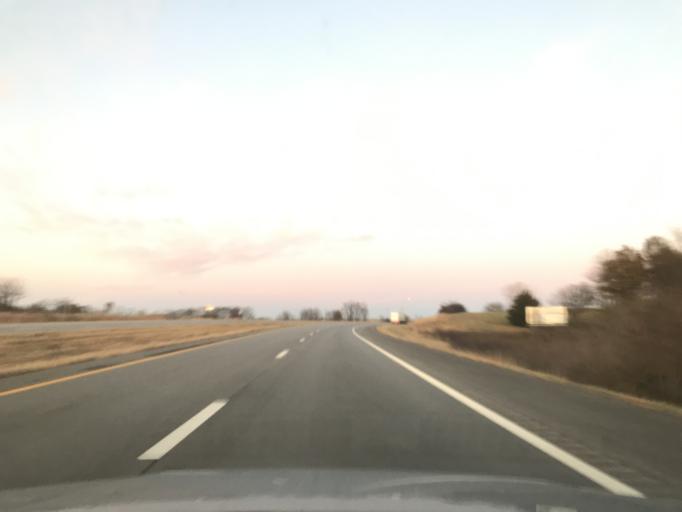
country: US
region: Missouri
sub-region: Marion County
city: Hannibal
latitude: 39.7115
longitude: -91.4554
